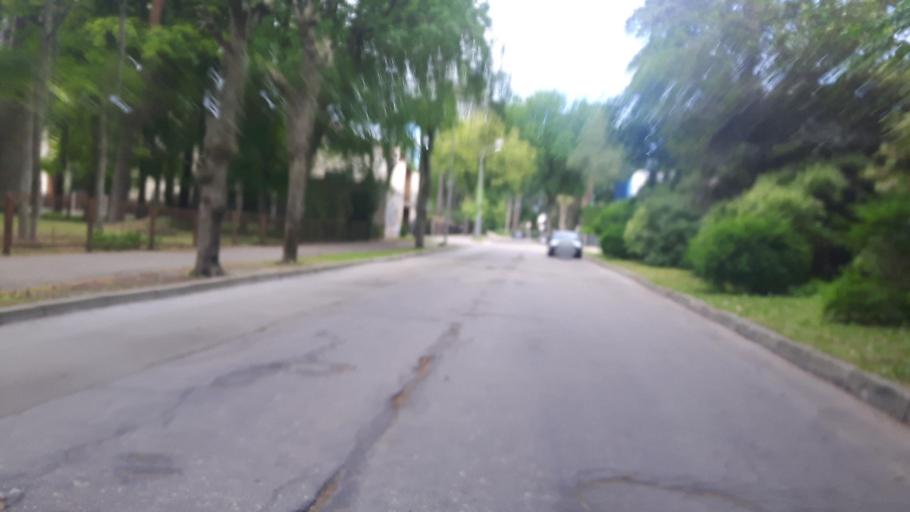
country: LV
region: Jurmala
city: Jurmala
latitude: 56.9783
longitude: 23.8260
